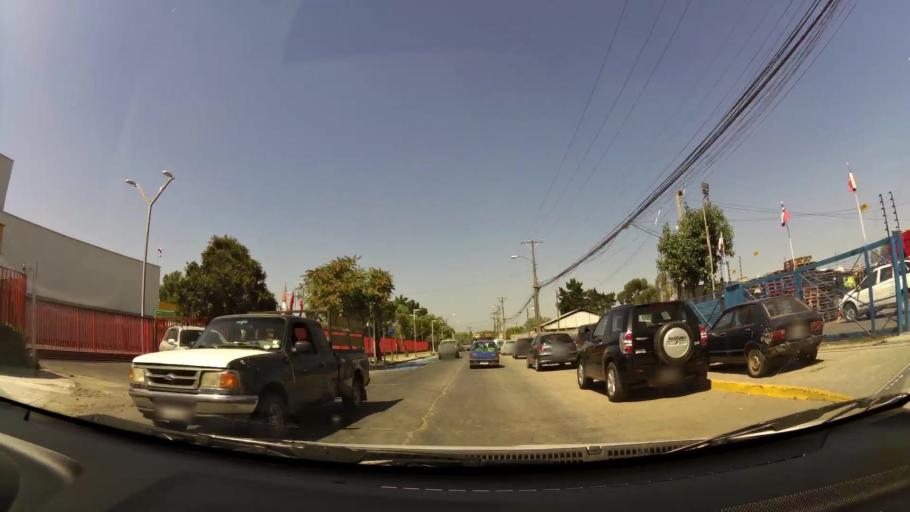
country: CL
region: Maule
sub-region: Provincia de Talca
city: Talca
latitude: -35.4224
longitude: -71.6368
